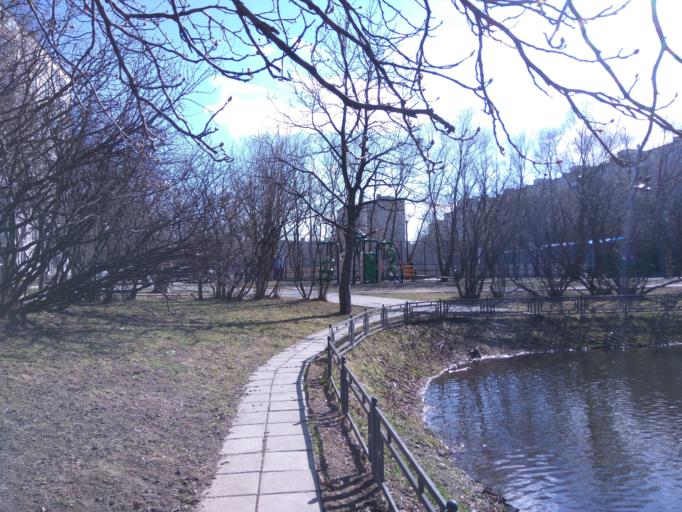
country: RU
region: Moscow
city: Ivanovskoye
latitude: 55.7712
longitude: 37.8387
